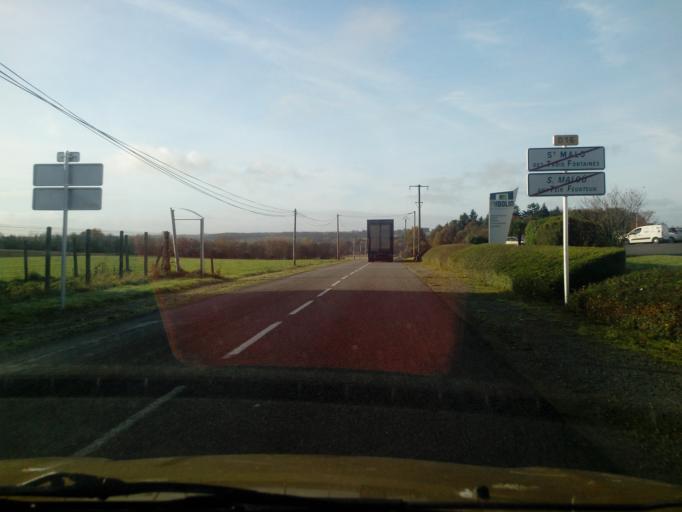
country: FR
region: Brittany
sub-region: Departement du Morbihan
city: Taupont
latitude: 48.0147
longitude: -2.4768
